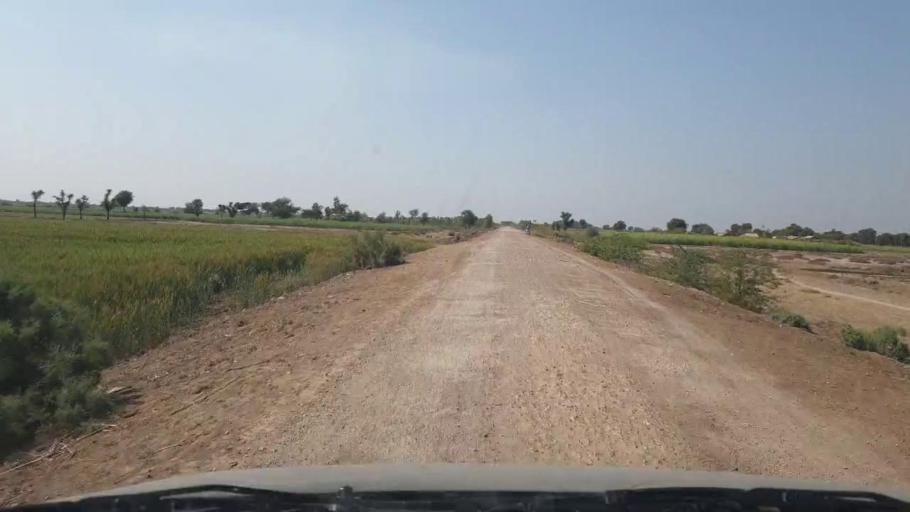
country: PK
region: Sindh
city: Samaro
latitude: 25.1920
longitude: 69.3496
